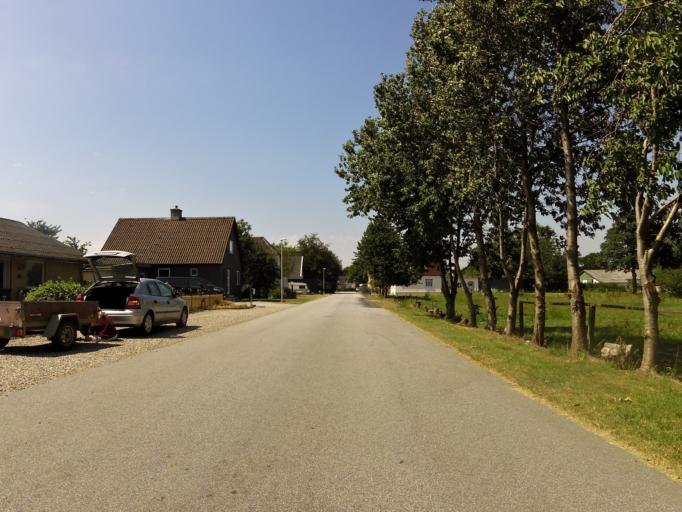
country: DK
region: South Denmark
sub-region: Haderslev Kommune
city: Vojens
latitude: 55.1582
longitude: 9.2551
